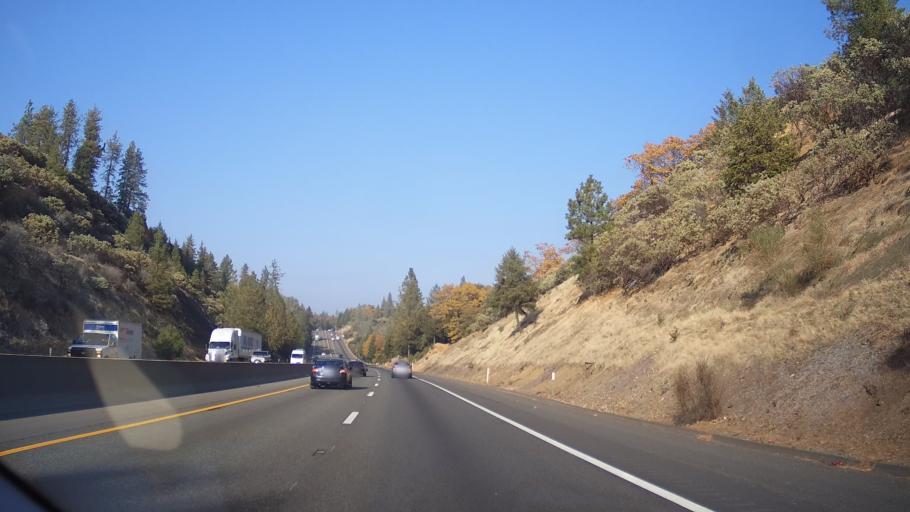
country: US
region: California
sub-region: Placer County
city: Colfax
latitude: 39.0522
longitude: -120.9705
